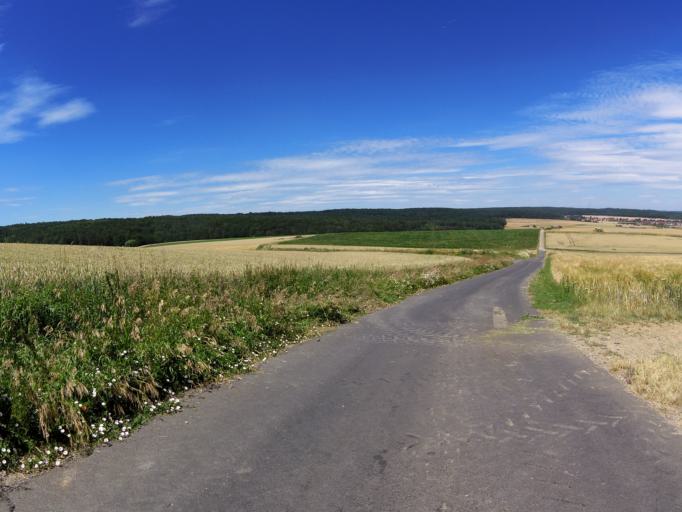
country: DE
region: Bavaria
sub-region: Regierungsbezirk Unterfranken
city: Geroldshausen
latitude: 49.7094
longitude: 9.9019
